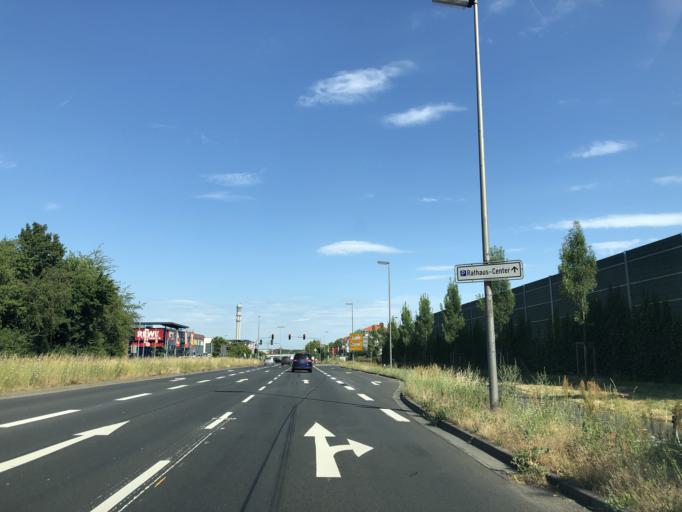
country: DE
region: Hesse
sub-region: Regierungsbezirk Darmstadt
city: Dietzenbach
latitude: 50.0182
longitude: 8.7788
